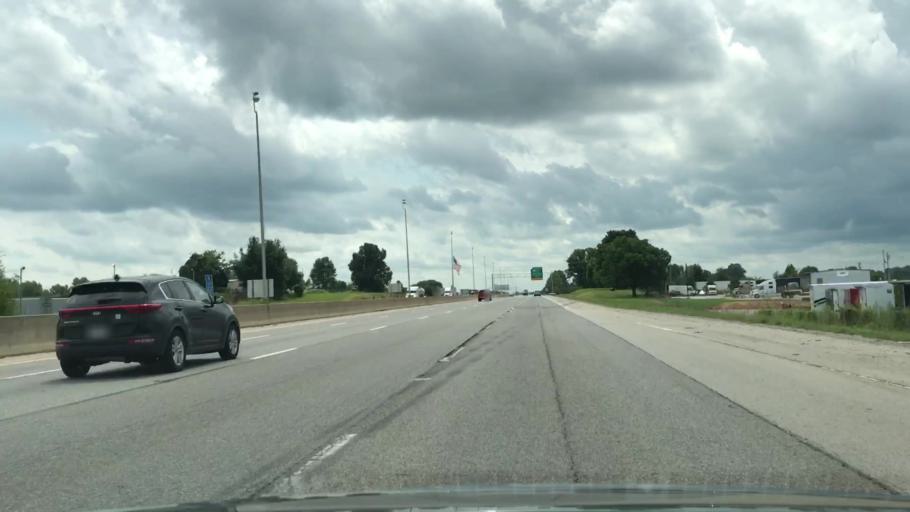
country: US
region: Kentucky
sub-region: Warren County
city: Plano
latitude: 36.9297
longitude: -86.4212
